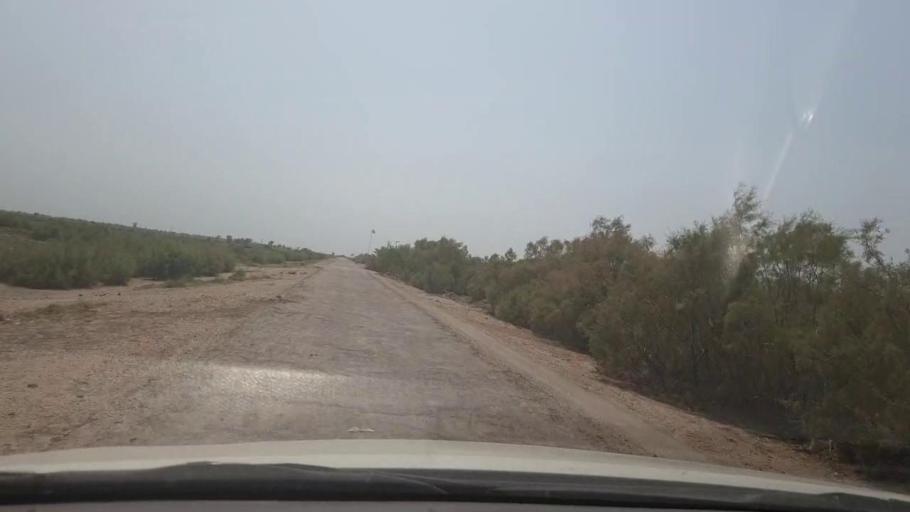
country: PK
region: Sindh
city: Garhi Yasin
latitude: 27.9914
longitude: 68.5185
